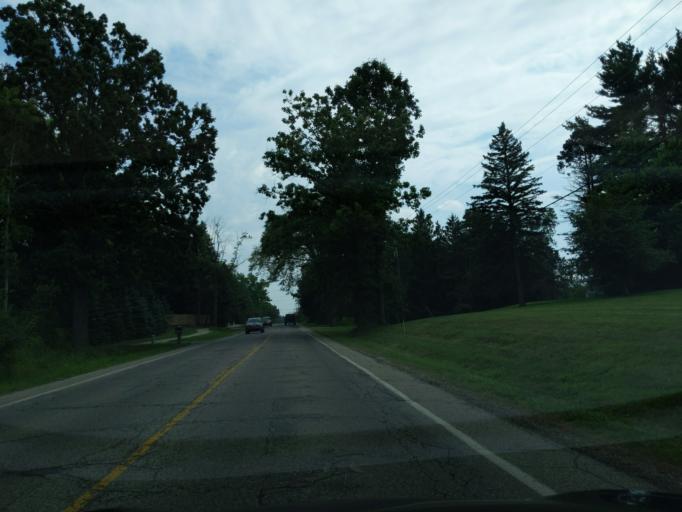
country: US
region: Michigan
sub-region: Ingham County
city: Okemos
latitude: 42.7303
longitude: -84.4276
